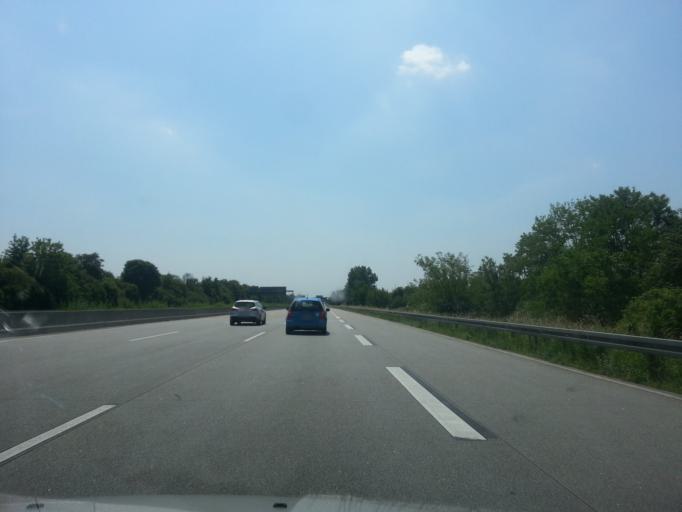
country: DE
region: Hesse
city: Viernheim
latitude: 49.5486
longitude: 8.5587
